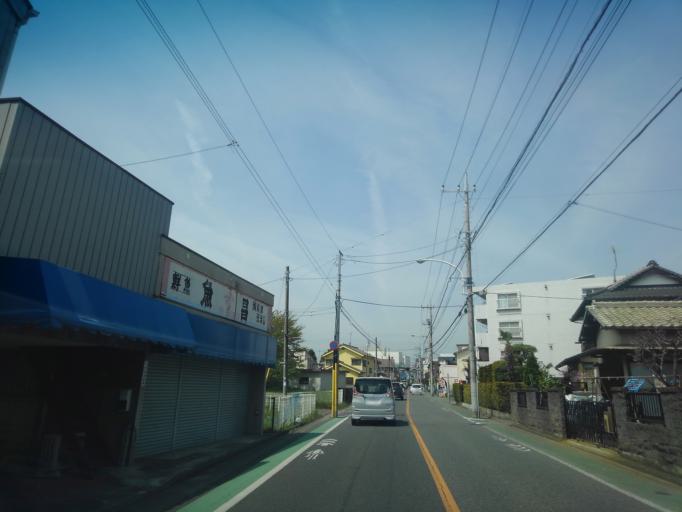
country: JP
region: Tokyo
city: Fussa
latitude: 35.7547
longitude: 139.3925
